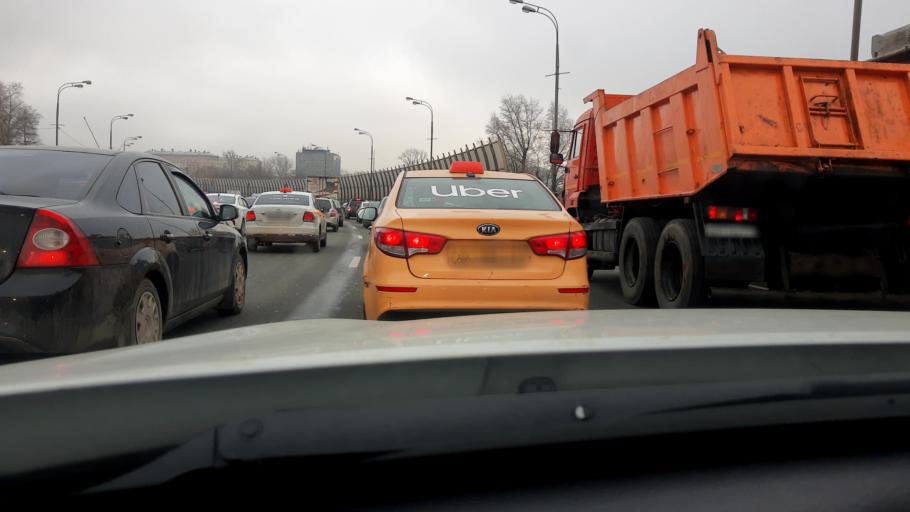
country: RU
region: Moscow
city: Novyye Cheremushki
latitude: 55.7023
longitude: 37.6108
